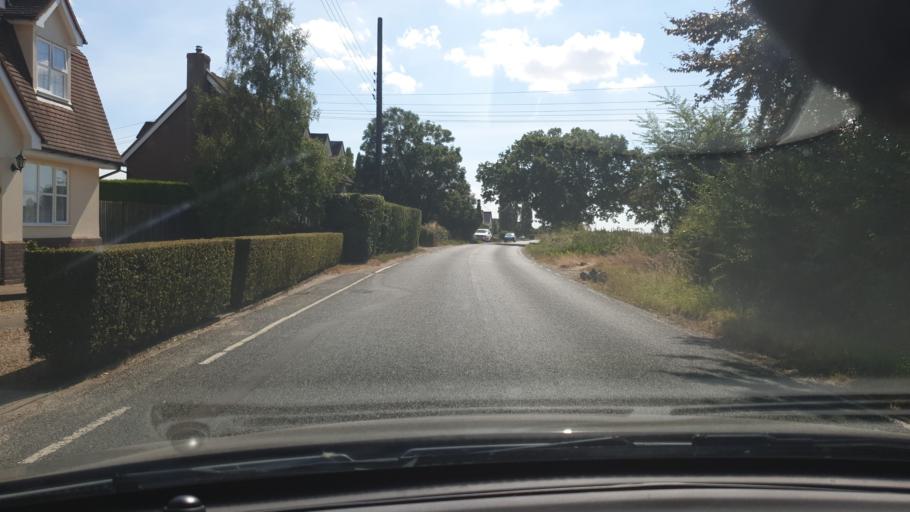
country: GB
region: England
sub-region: Essex
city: Mistley
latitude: 51.9183
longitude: 1.1401
